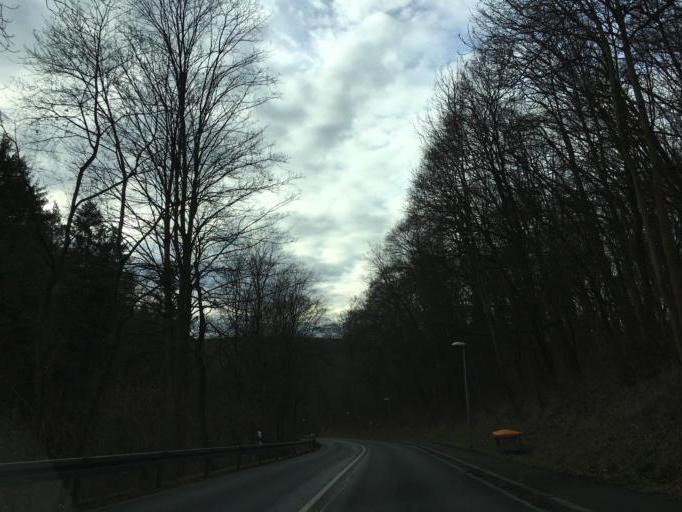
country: DE
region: Thuringia
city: Hetschburg
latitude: 50.9300
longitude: 11.2916
